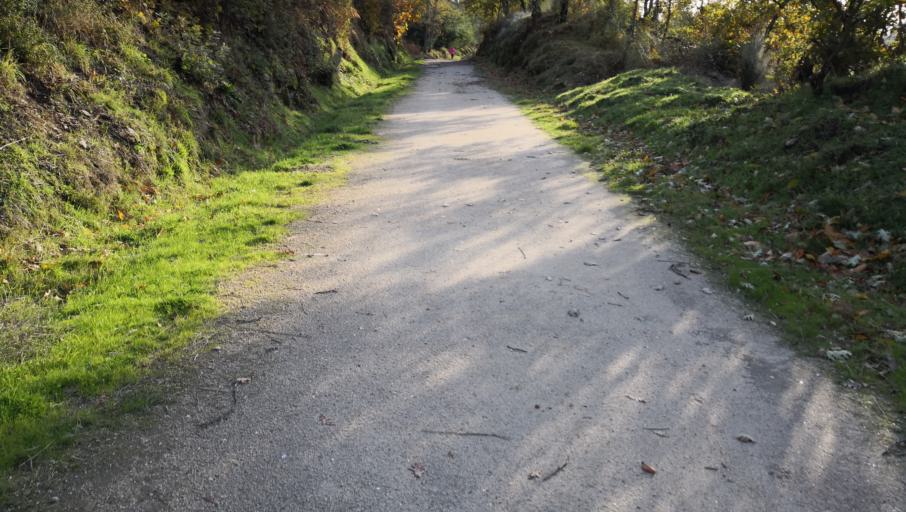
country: PT
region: Vila Real
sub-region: Vila Real
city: Vila Real
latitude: 41.3246
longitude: -7.7106
